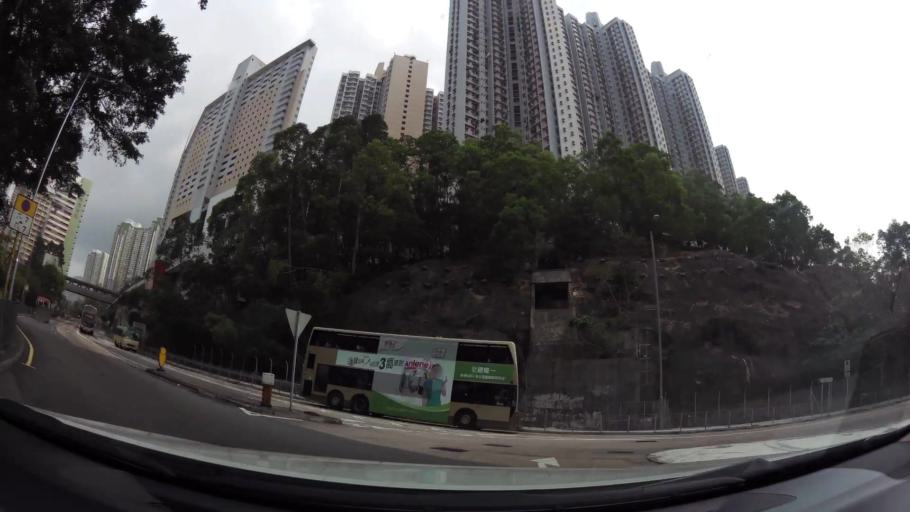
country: HK
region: Kowloon City
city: Kowloon
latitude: 22.3157
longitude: 114.2365
